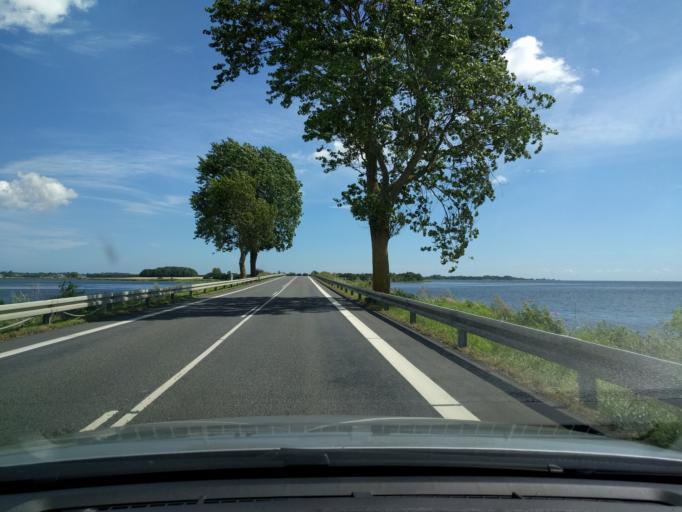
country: DK
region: Zealand
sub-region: Guldborgsund Kommune
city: Stubbekobing
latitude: 54.9061
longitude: 12.0965
